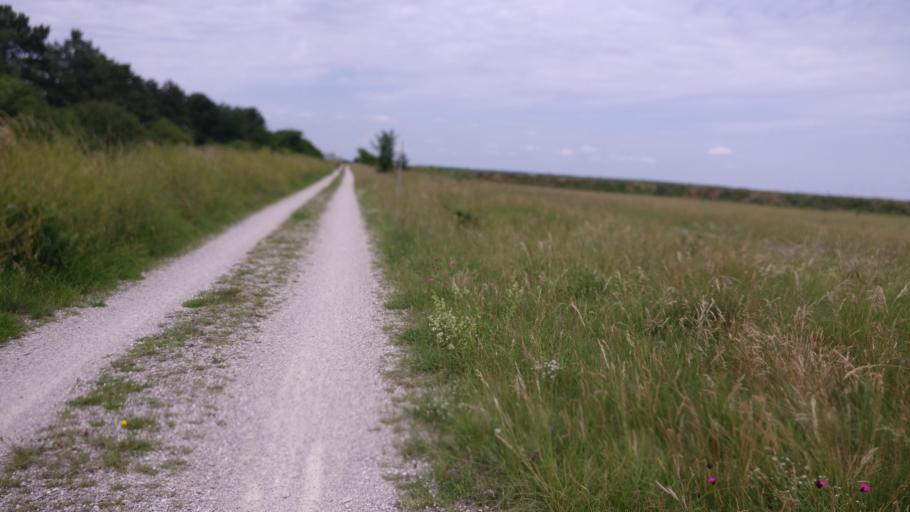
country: AT
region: Lower Austria
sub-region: Politischer Bezirk Wiener Neustadt
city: Sollenau
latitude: 47.8695
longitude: 16.2816
